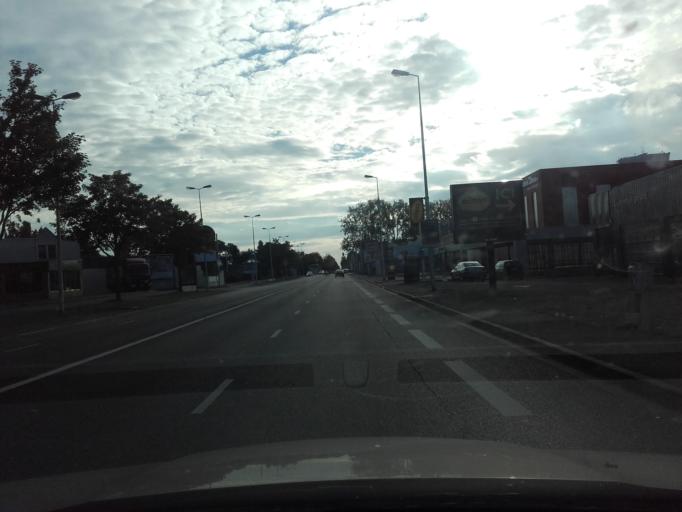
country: FR
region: Centre
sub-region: Departement d'Indre-et-Loire
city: Saint-Cyr-sur-Loire
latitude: 47.4256
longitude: 0.7003
